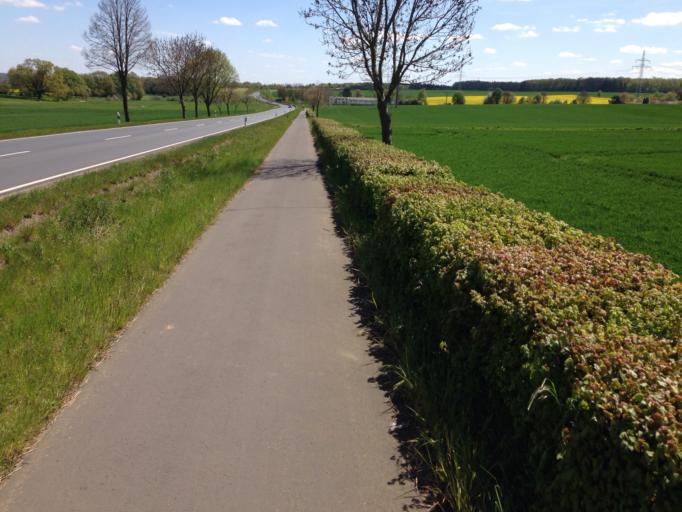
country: DE
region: Hesse
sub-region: Regierungsbezirk Giessen
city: Hungen
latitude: 50.4816
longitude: 8.8697
